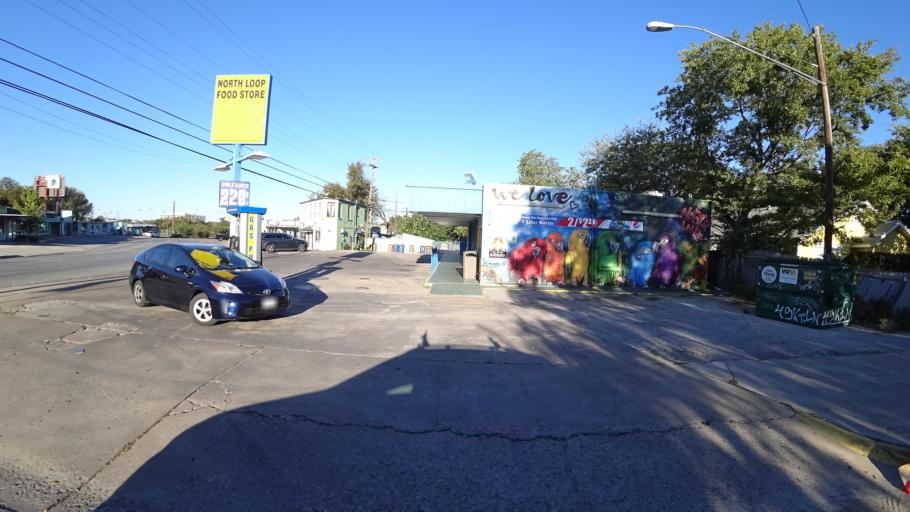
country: US
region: Texas
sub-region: Travis County
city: Austin
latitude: 30.3179
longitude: -97.7211
